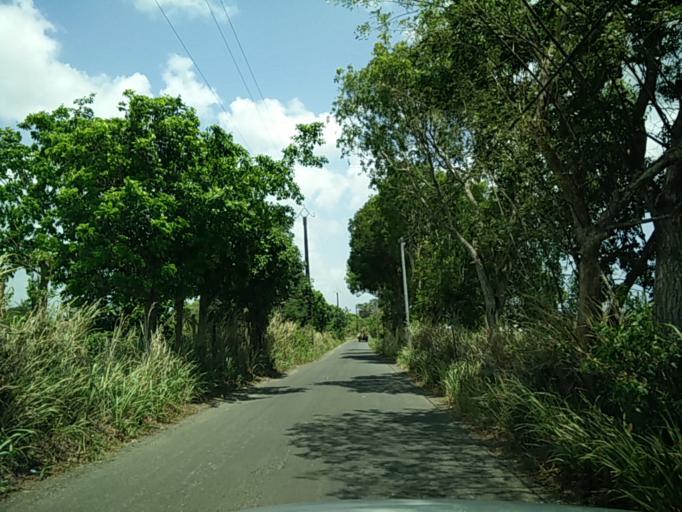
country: GP
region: Guadeloupe
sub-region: Guadeloupe
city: Les Abymes
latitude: 16.2804
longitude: -61.5135
